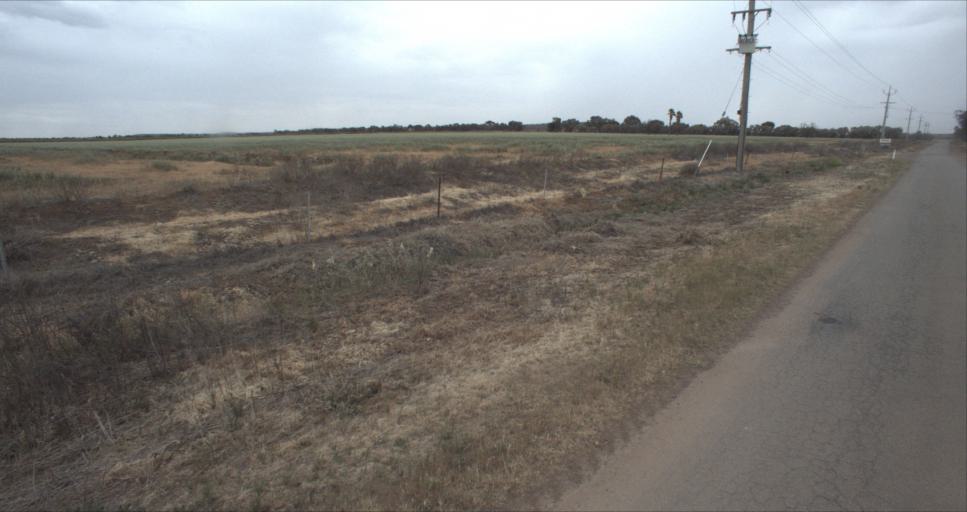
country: AU
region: New South Wales
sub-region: Leeton
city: Leeton
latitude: -34.4075
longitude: 146.3410
